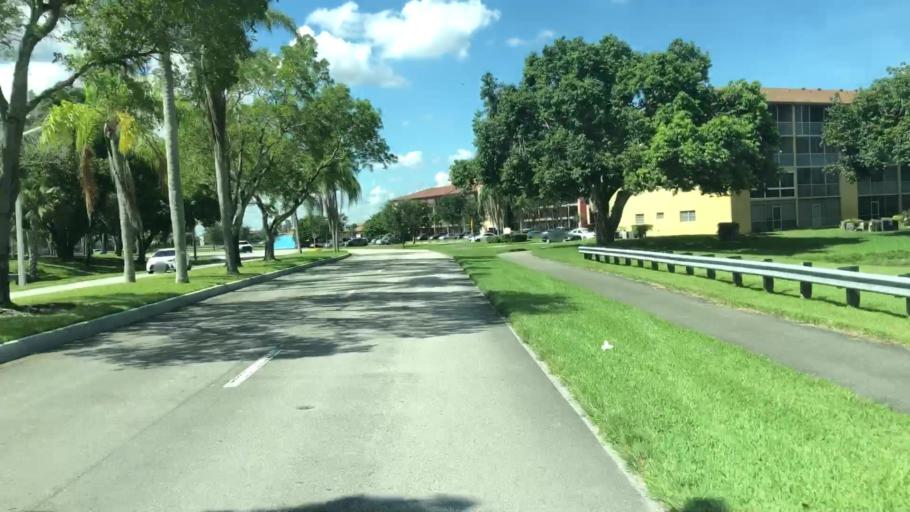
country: US
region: Florida
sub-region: Broward County
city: Sunshine Ranches
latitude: 26.0022
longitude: -80.3215
